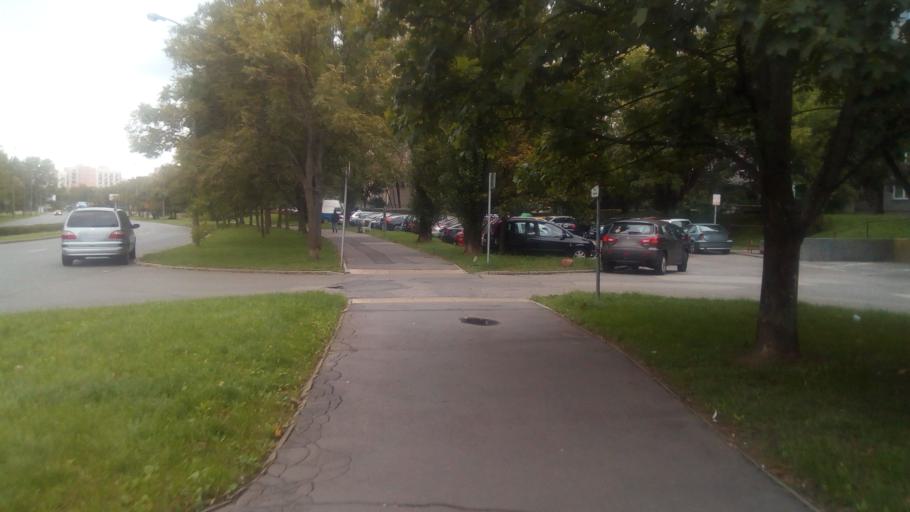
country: PL
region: Masovian Voivodeship
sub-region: Warszawa
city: Ursynow
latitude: 52.1515
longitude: 21.0487
